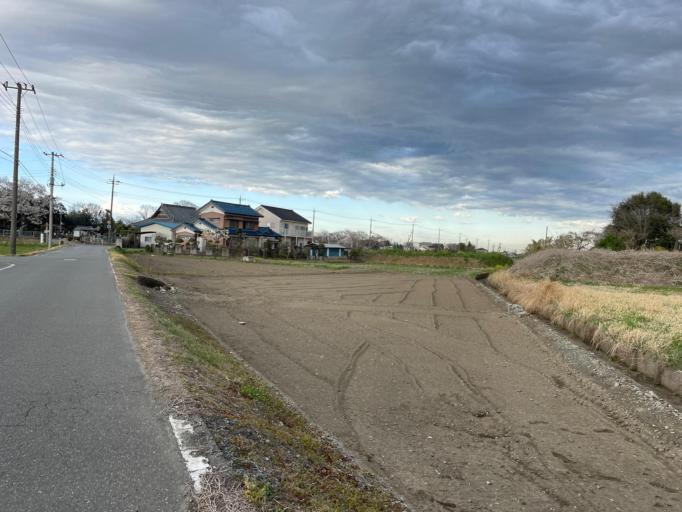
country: JP
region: Saitama
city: Fukayacho
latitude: 36.1303
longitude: 139.2687
